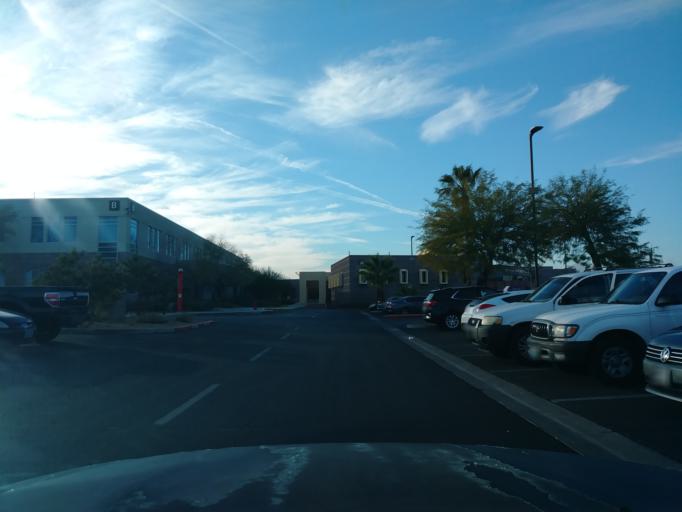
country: US
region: Nevada
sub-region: Clark County
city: Spring Valley
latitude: 36.1584
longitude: -115.2321
